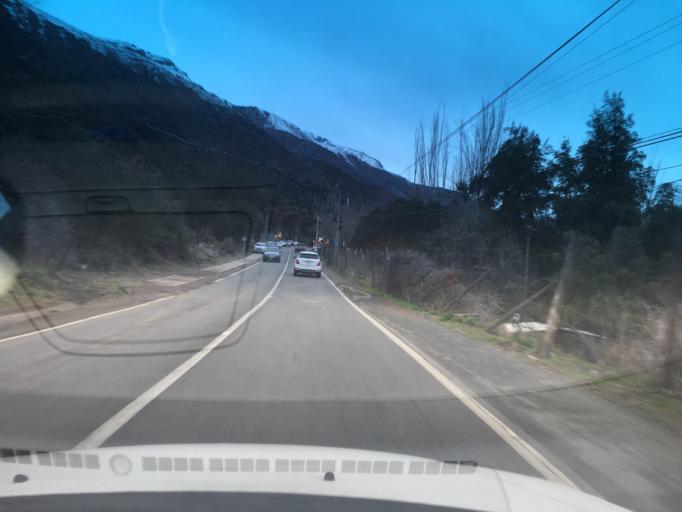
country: CL
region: Santiago Metropolitan
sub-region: Provincia de Cordillera
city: Puente Alto
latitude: -33.6762
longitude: -70.3424
